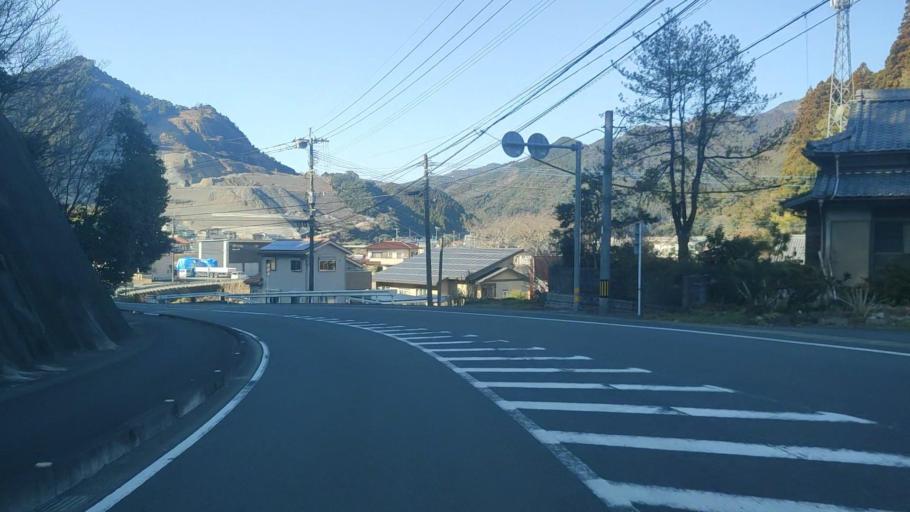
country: JP
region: Oita
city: Saiki
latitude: 32.9766
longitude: 131.8531
